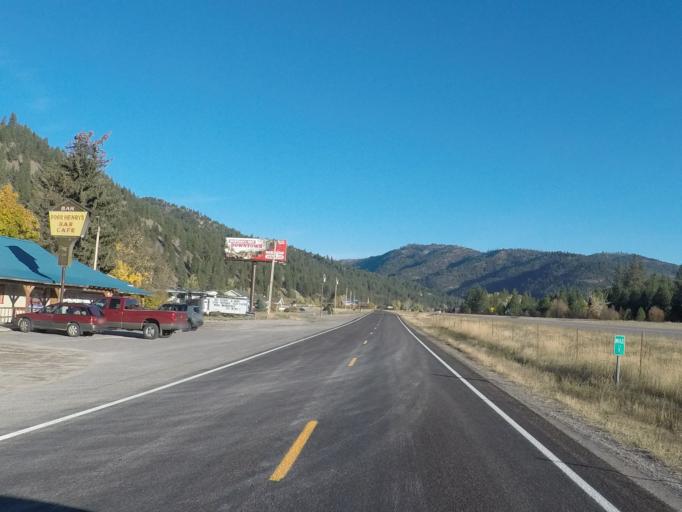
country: US
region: Montana
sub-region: Missoula County
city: Clinton
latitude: 46.7903
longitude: -113.7307
